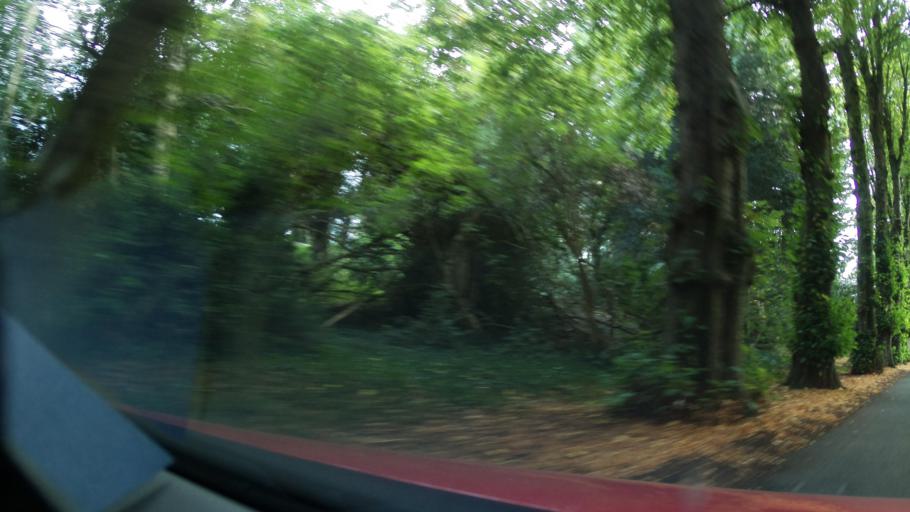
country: GB
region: England
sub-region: Staffordshire
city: Barlaston
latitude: 52.9478
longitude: -2.1576
